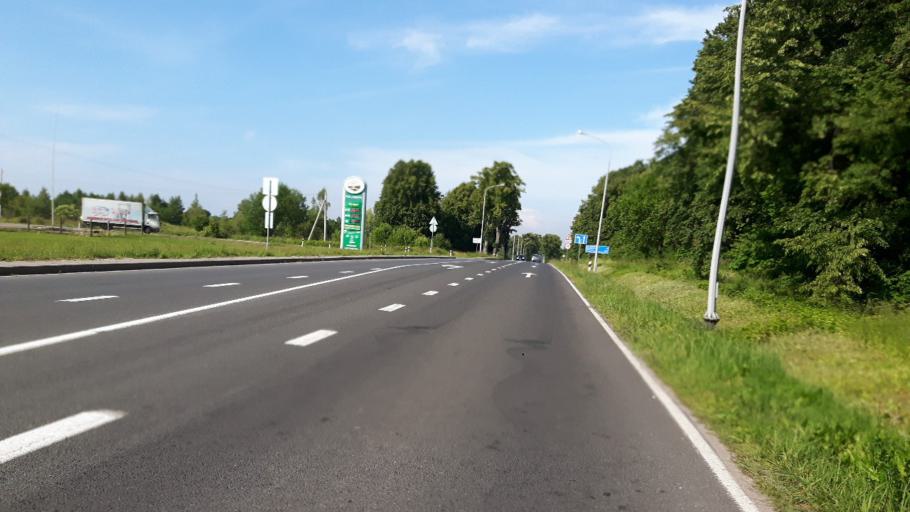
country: RU
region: Kaliningrad
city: Mamonovo
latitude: 54.4513
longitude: 19.9185
